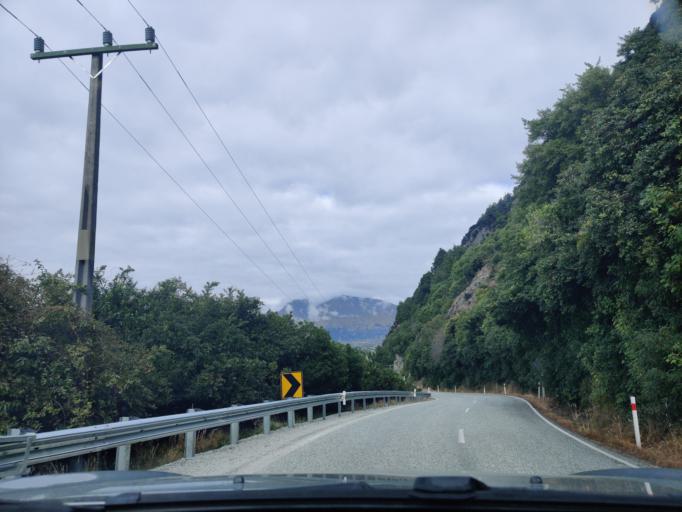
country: NZ
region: Otago
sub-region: Queenstown-Lakes District
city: Queenstown
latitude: -45.0761
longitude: 168.4911
